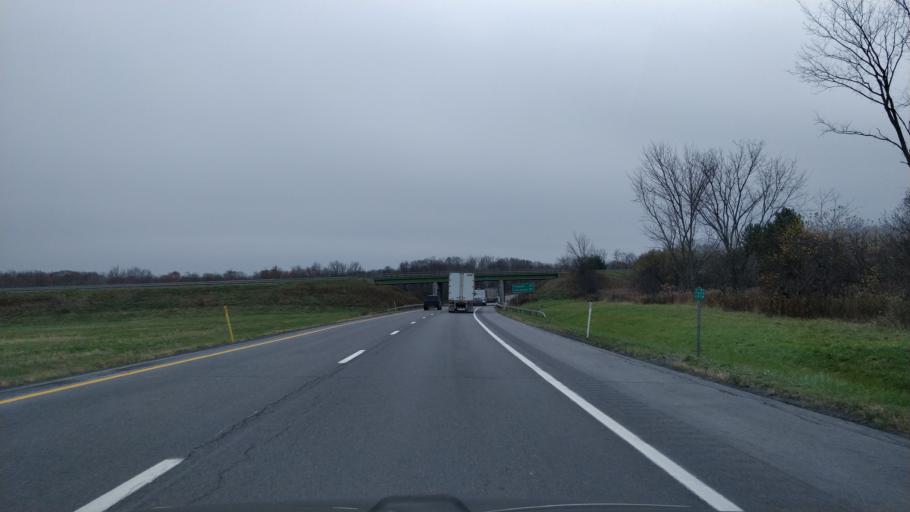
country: US
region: New York
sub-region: Jefferson County
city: Adams
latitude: 43.7788
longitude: -76.0439
